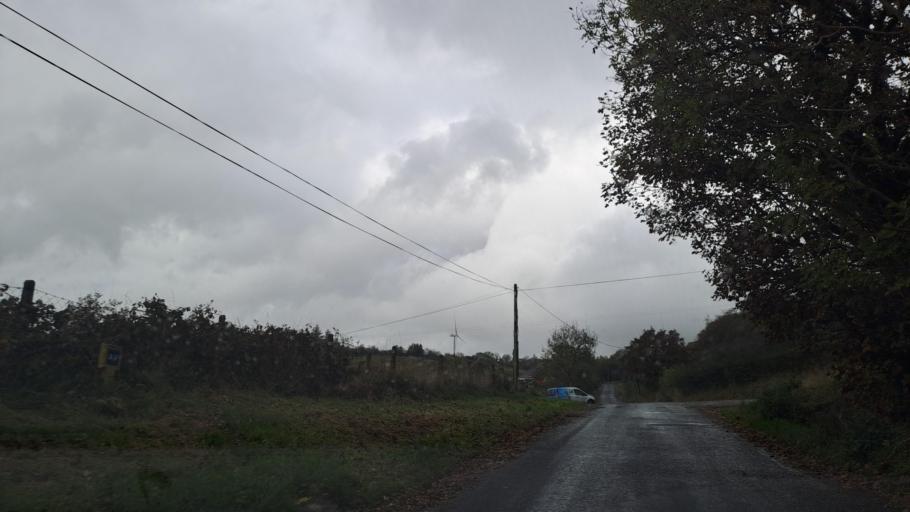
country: IE
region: Ulster
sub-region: An Cabhan
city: Bailieborough
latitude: 53.9406
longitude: -6.9094
